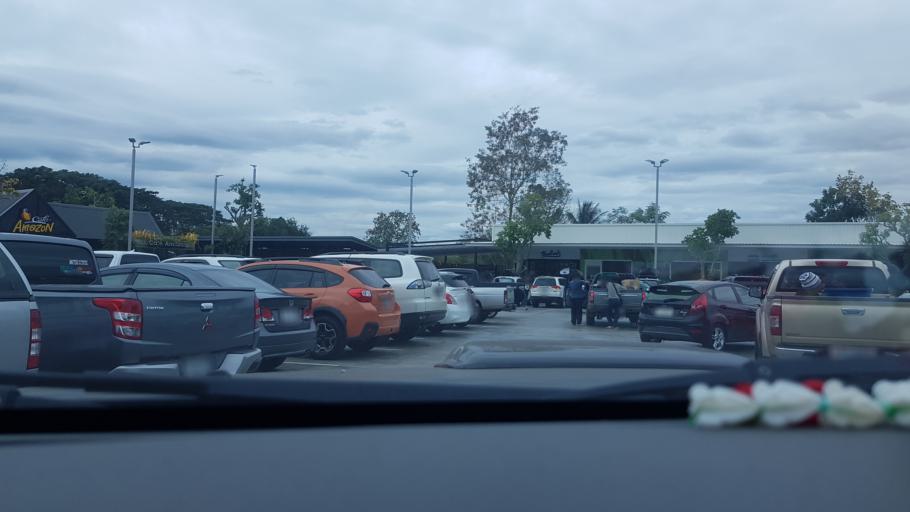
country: TH
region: Phetchabun
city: Phetchabun
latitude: 16.4999
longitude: 101.1567
